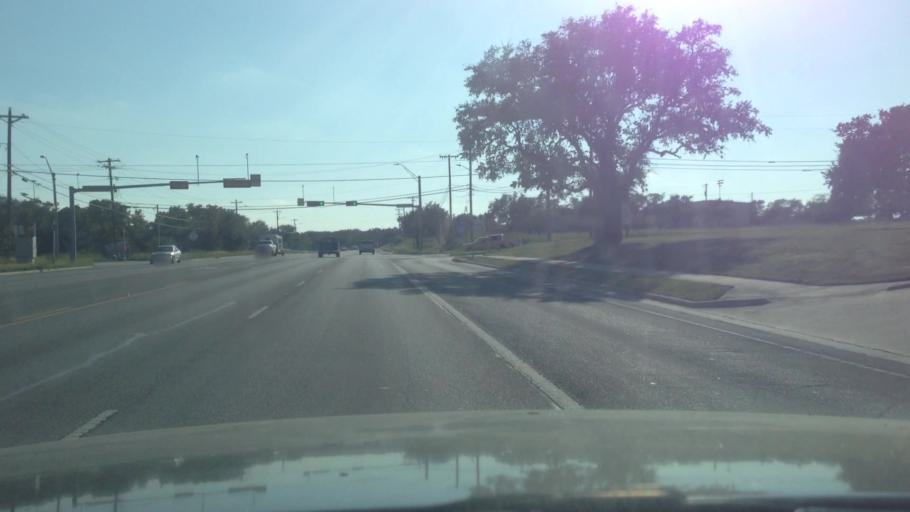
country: US
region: Texas
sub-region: Hays County
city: San Marcos
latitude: 29.8581
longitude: -97.9689
